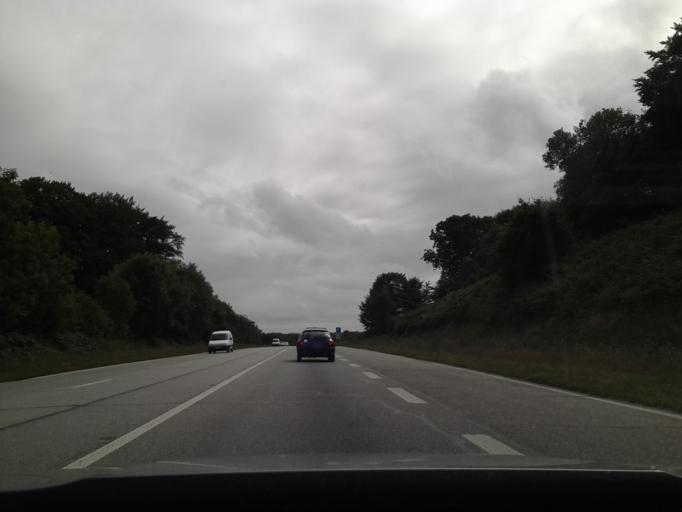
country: FR
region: Lower Normandy
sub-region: Departement de la Manche
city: La Glacerie
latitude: 49.6167
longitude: -1.5825
